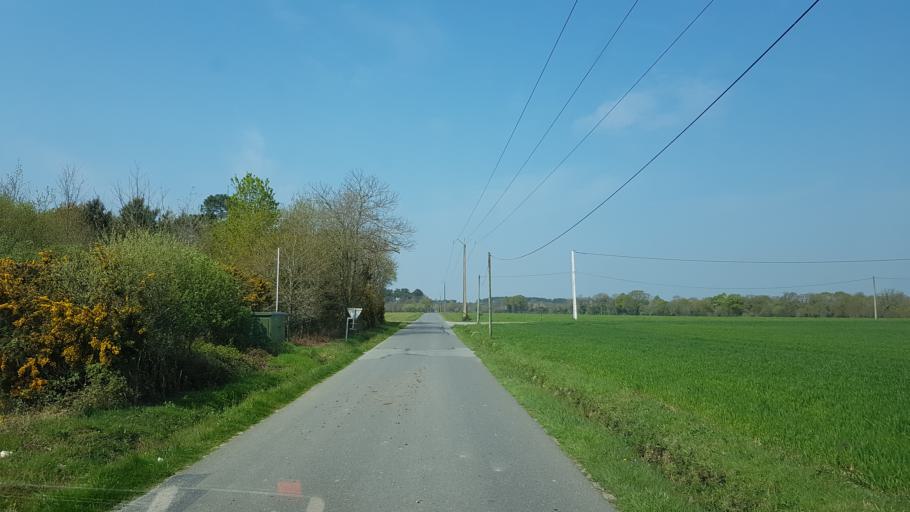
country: FR
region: Brittany
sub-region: Departement du Morbihan
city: Peaule
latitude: 47.5857
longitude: -2.3778
